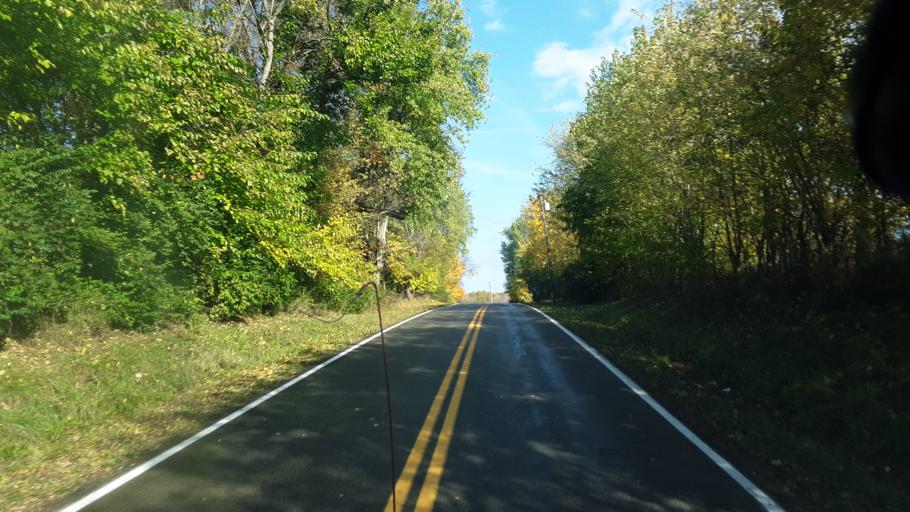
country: US
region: Ohio
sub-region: Highland County
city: Leesburg
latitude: 39.3404
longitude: -83.5843
